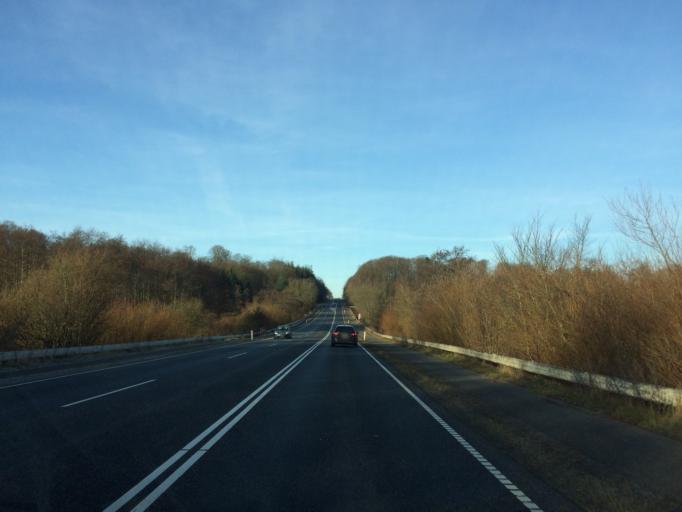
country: DK
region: South Denmark
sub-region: Vejle Kommune
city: Borkop
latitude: 55.5880
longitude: 9.6502
